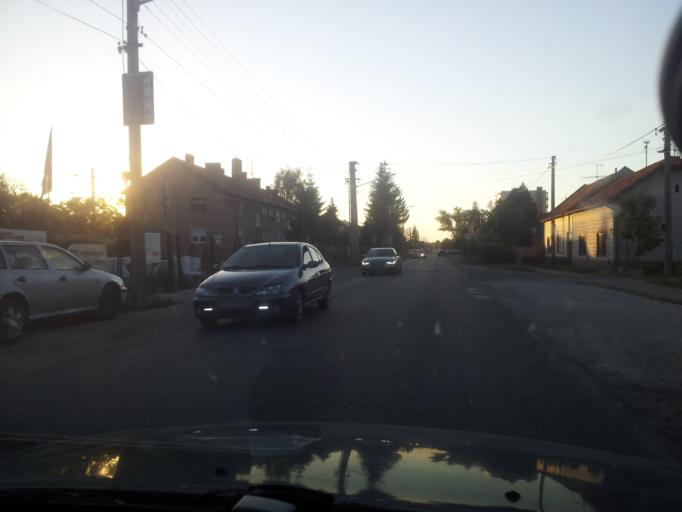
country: SK
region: Nitriansky
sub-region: Okres Nove Zamky
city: Sturovo
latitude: 47.8017
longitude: 18.7124
